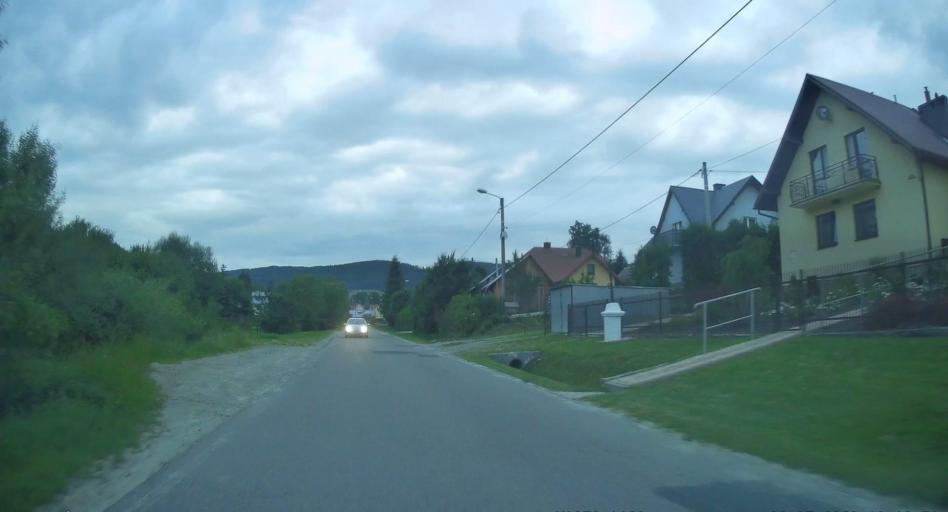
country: PL
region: Lesser Poland Voivodeship
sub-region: Powiat nowosadecki
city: Muszyna
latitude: 49.3821
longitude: 20.9217
